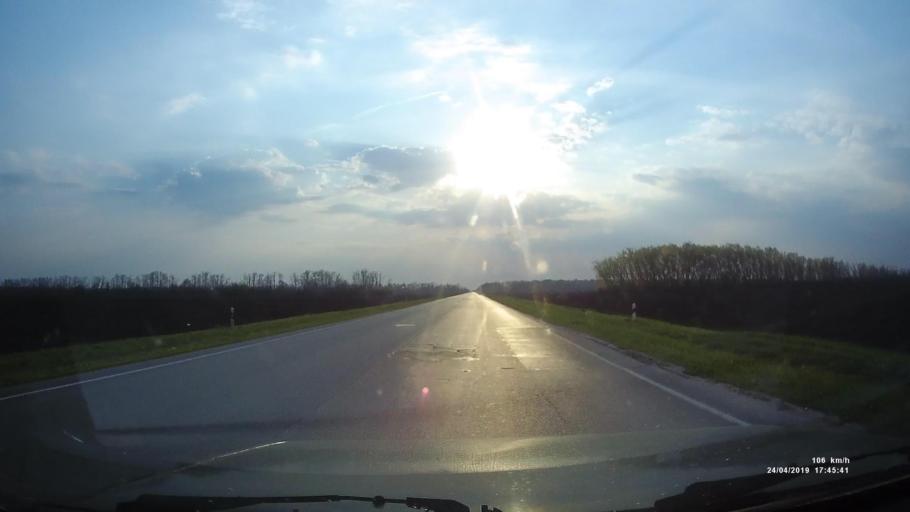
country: RU
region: Rostov
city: Tselina
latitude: 46.5363
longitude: 40.8850
